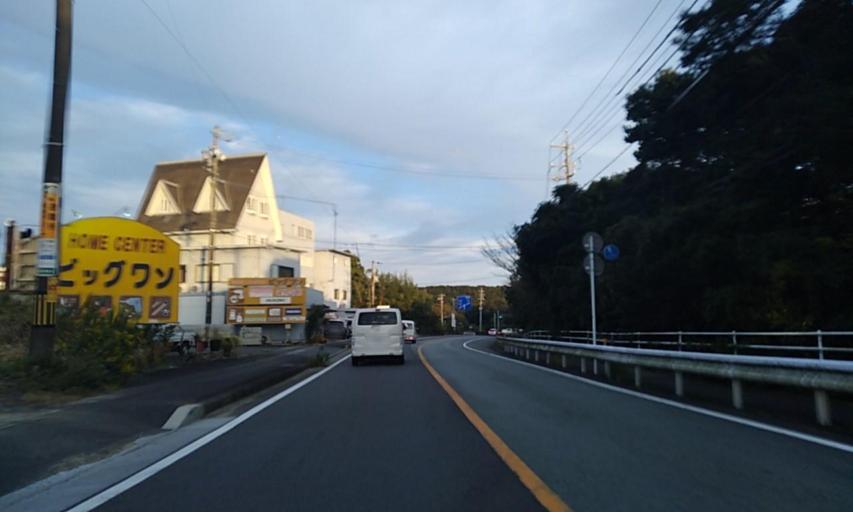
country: JP
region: Mie
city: Toba
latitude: 34.3240
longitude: 136.8458
